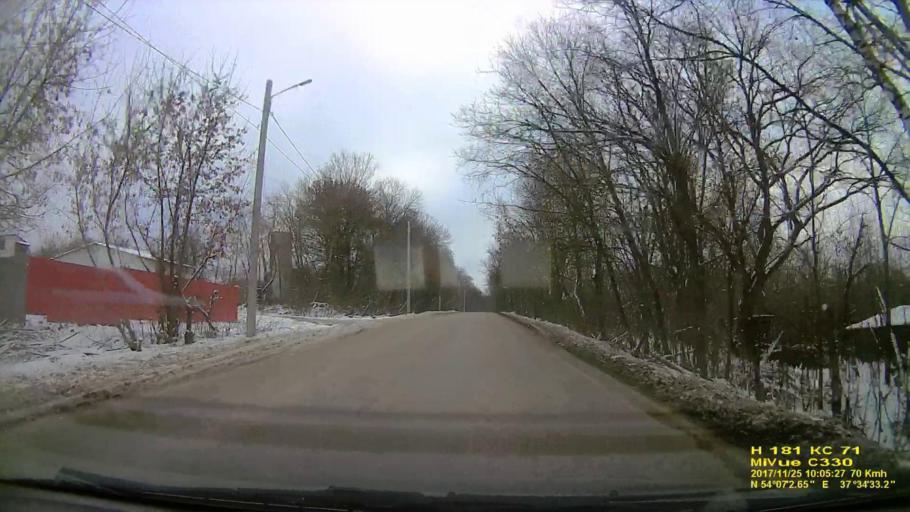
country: RU
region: Tula
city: Mendeleyevskiy
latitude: 54.1174
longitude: 37.5763
